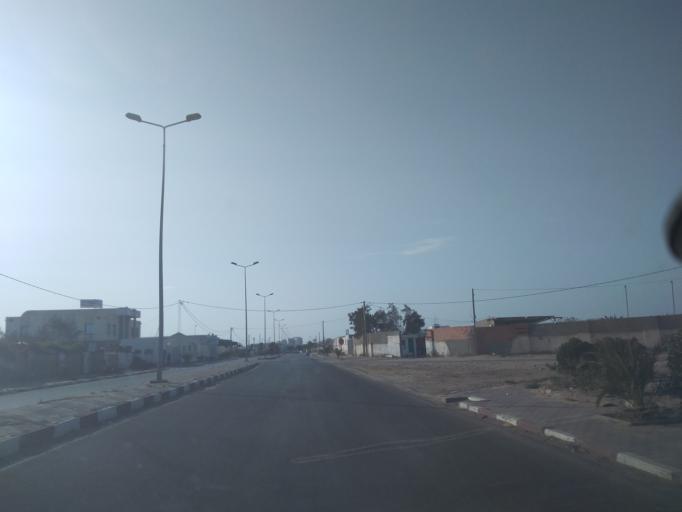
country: TN
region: Safaqis
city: Sfax
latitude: 34.7220
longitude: 10.7602
